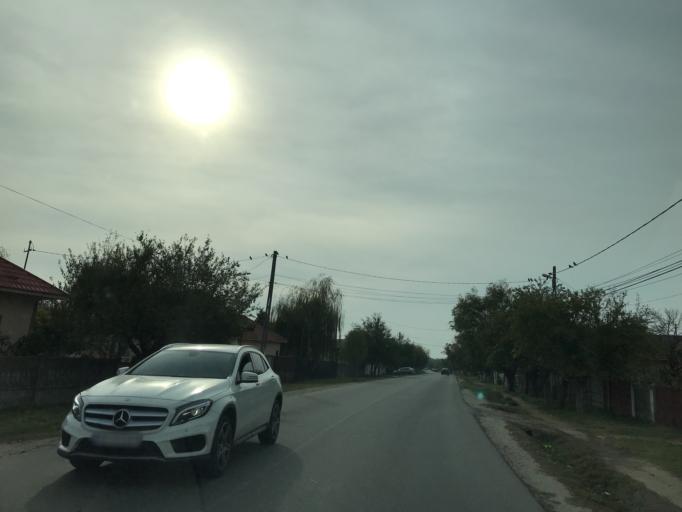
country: RO
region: Olt
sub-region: Comuna Piatra Olt
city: Piatra
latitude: 44.3698
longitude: 24.3121
